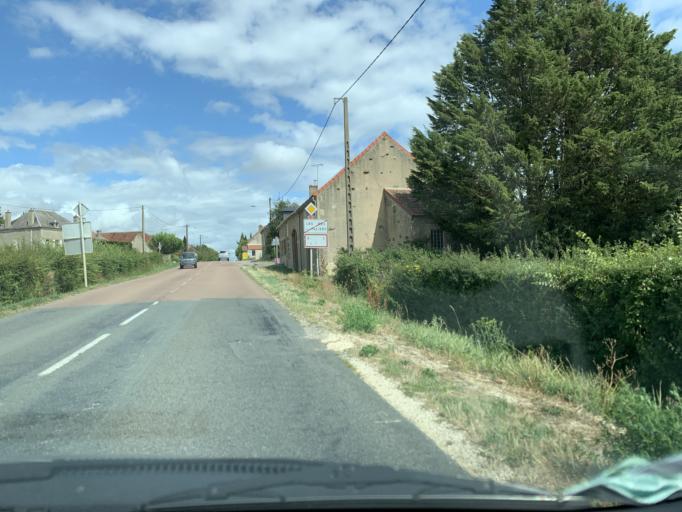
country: FR
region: Bourgogne
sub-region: Departement de la Nievre
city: Varzy
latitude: 47.3754
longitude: 3.4286
